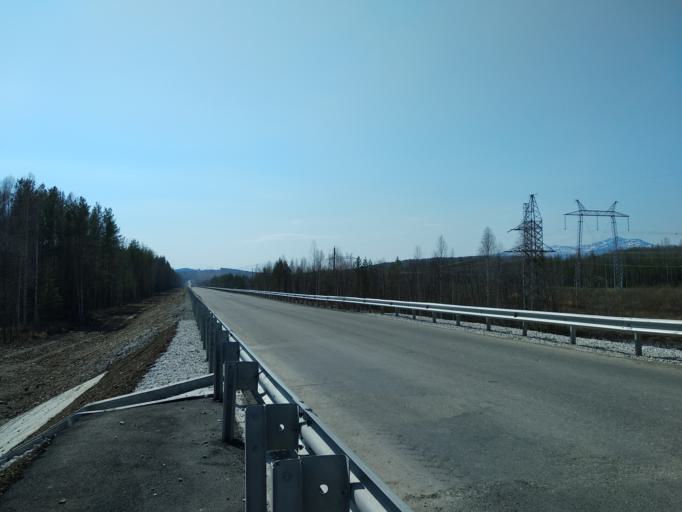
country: RU
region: Sverdlovsk
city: Karpinsk
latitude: 59.5990
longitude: 59.5039
